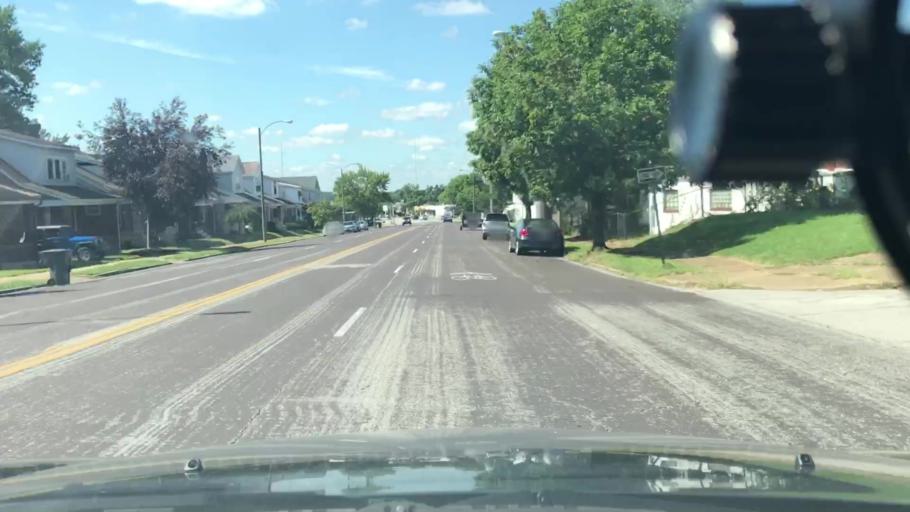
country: US
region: Missouri
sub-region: Saint Louis County
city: Maplewood
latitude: 38.6089
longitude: -90.2906
